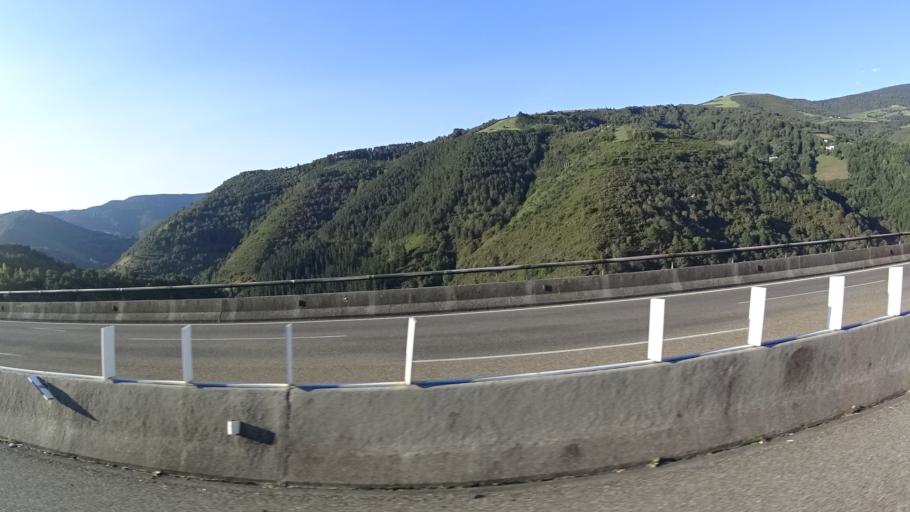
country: ES
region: Galicia
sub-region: Provincia de Lugo
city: San Roman
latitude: 42.7498
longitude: -7.0598
